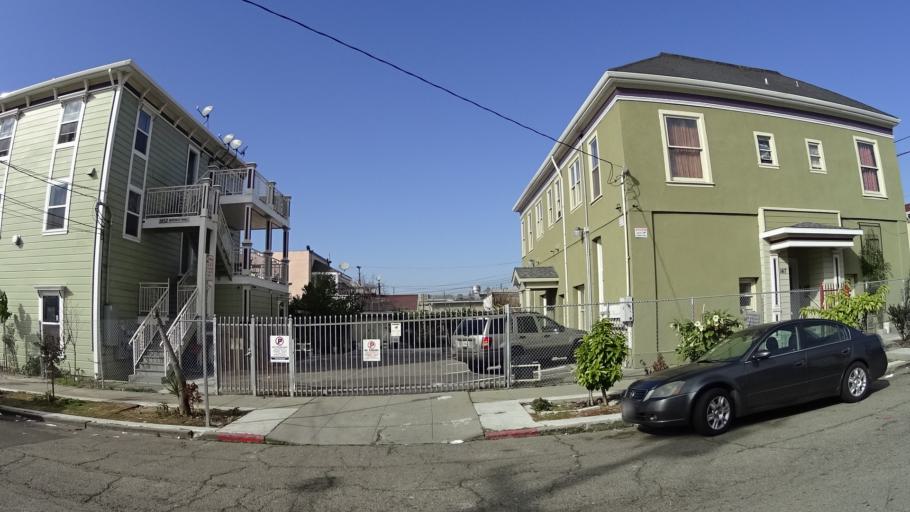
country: US
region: California
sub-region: Alameda County
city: Alameda
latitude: 37.7861
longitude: -122.2397
